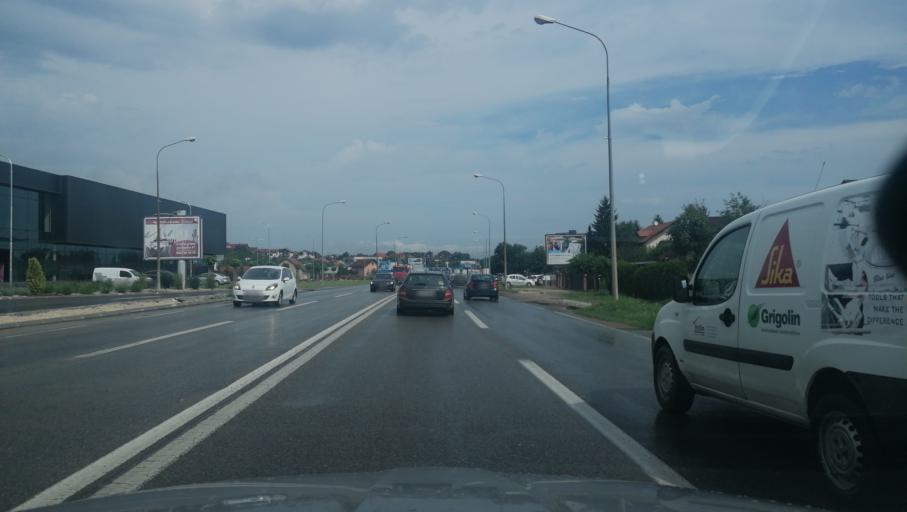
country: BA
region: Republika Srpska
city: Banja Luka
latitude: 44.8060
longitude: 17.1982
